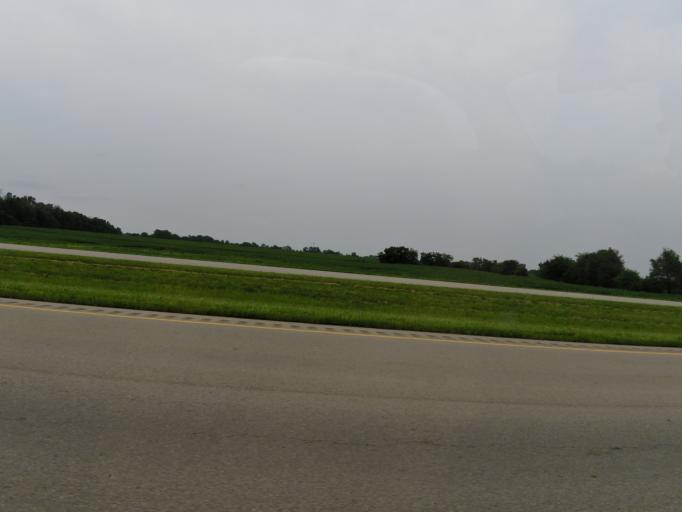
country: US
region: Ohio
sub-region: Clinton County
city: Wilmington
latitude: 39.4646
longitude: -83.8425
